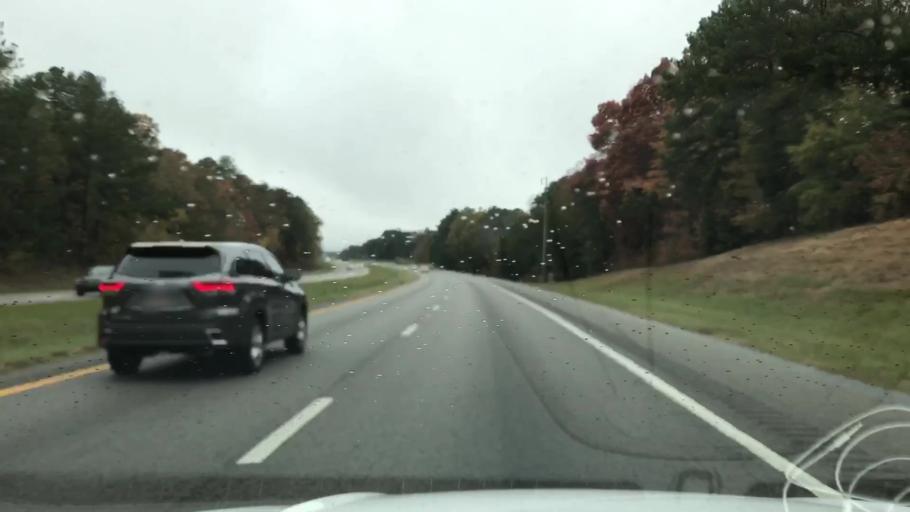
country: US
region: South Carolina
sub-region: Lexington County
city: Irmo
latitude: 34.1333
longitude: -81.2104
